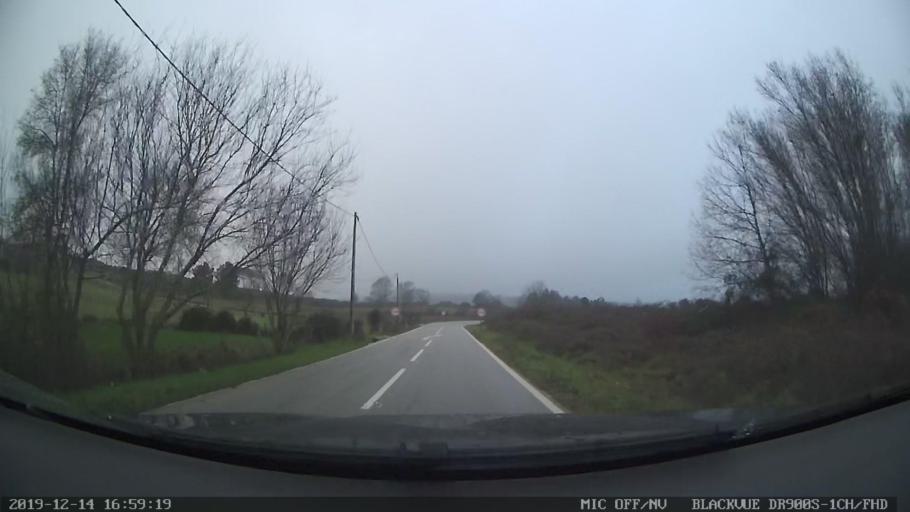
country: PT
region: Vila Real
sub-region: Vila Pouca de Aguiar
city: Vila Pouca de Aguiar
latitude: 41.4354
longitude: -7.5615
